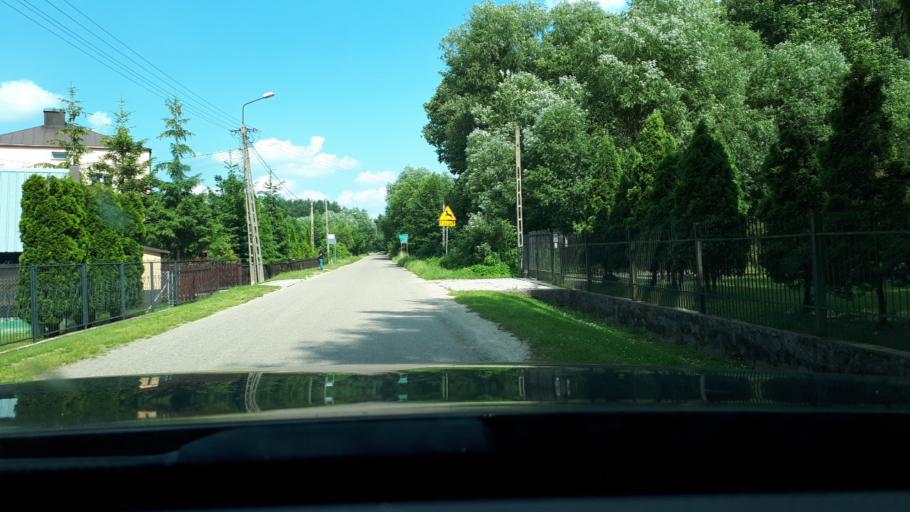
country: PL
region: Podlasie
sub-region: Powiat bialostocki
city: Choroszcz
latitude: 53.1300
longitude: 22.8826
